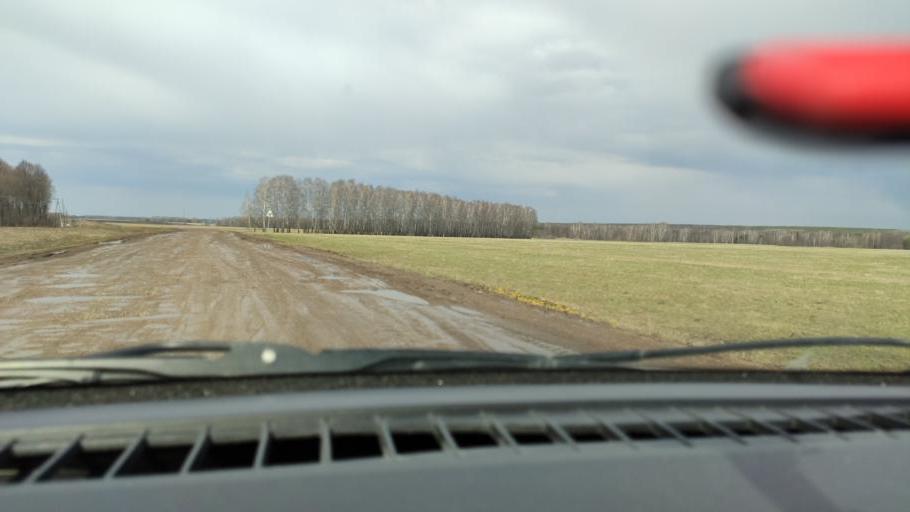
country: RU
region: Bashkortostan
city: Burayevo
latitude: 55.6530
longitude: 55.1887
